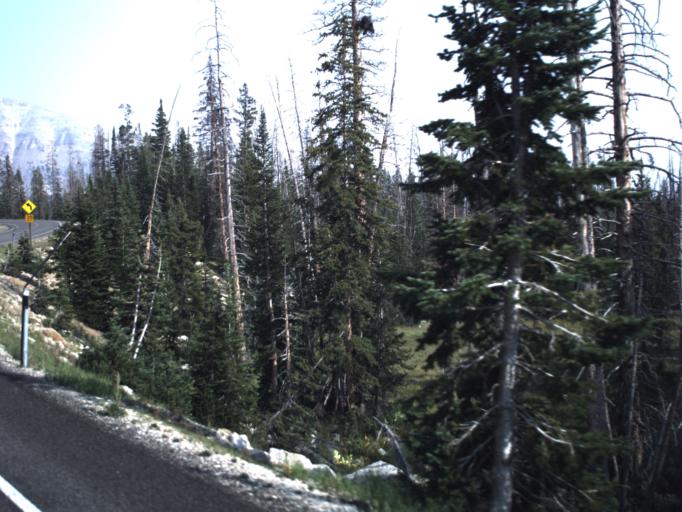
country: US
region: Utah
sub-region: Summit County
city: Kamas
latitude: 40.7195
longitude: -110.8760
